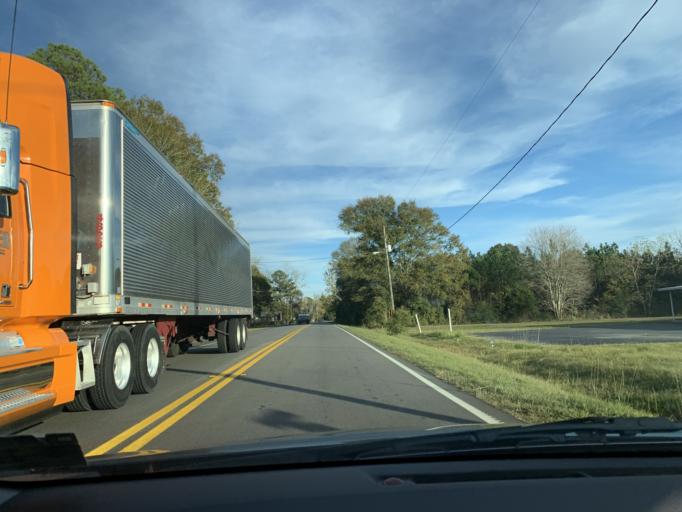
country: US
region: Georgia
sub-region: Irwin County
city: Ocilla
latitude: 31.5941
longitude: -83.2437
